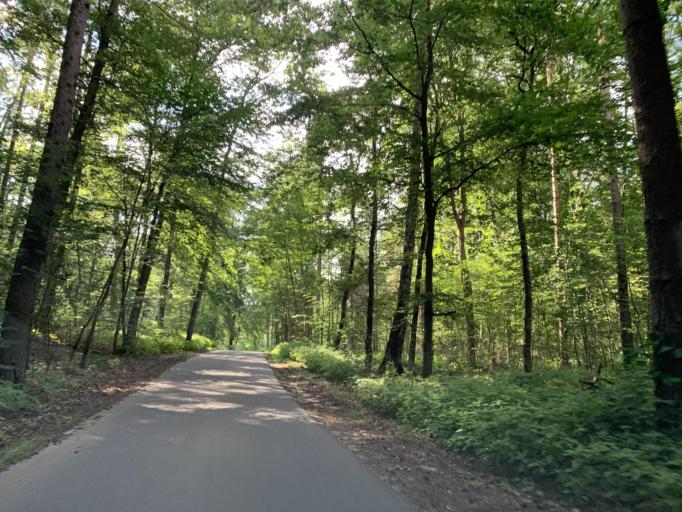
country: DE
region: Mecklenburg-Vorpommern
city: Carpin
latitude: 53.3837
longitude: 13.2133
